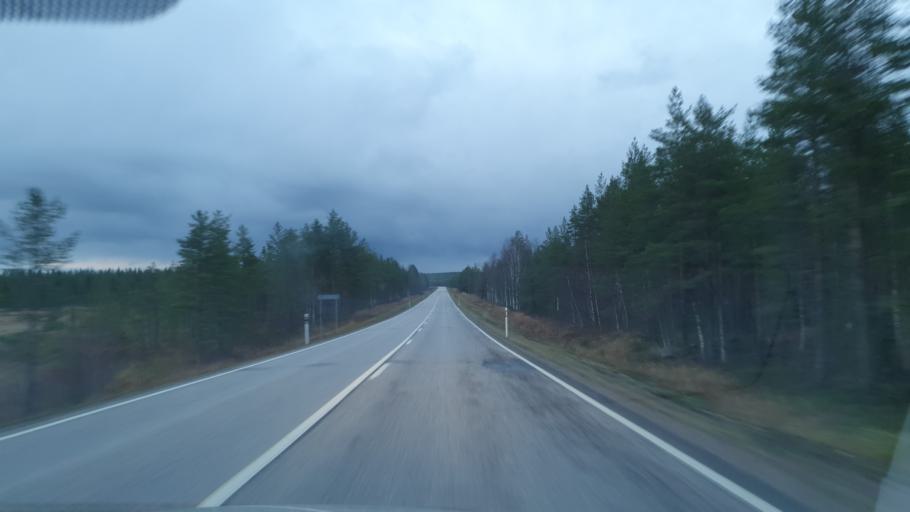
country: FI
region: Kainuu
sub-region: Kehys-Kainuu
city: Hyrynsalmi
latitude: 64.6122
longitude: 28.4727
